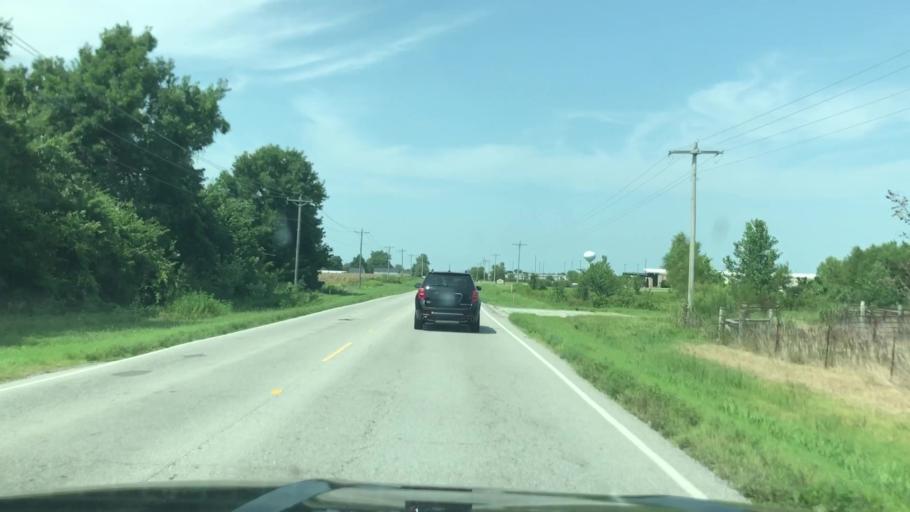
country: US
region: Oklahoma
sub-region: Ottawa County
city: Commerce
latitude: 36.9034
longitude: -94.8419
